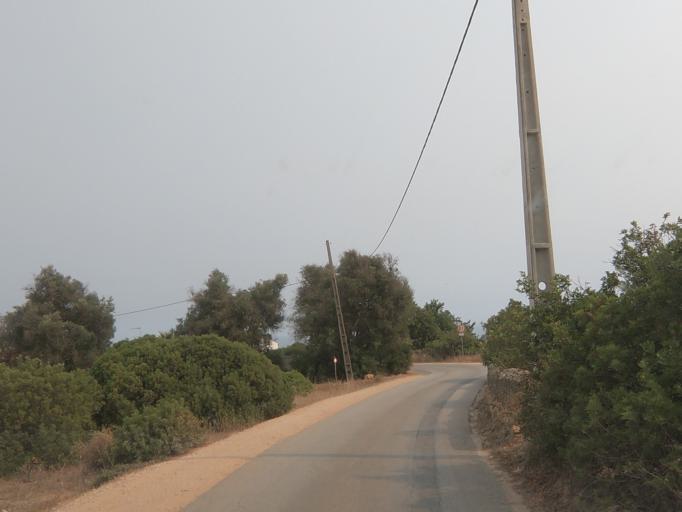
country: PT
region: Faro
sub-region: Lagoa
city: Carvoeiro
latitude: 37.0965
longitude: -8.4092
